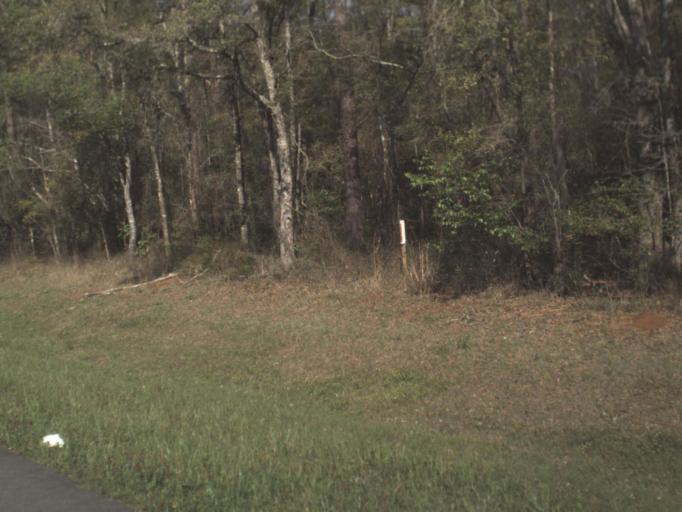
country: US
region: Alabama
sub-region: Houston County
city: Cottonwood
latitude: 30.9346
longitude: -85.2999
